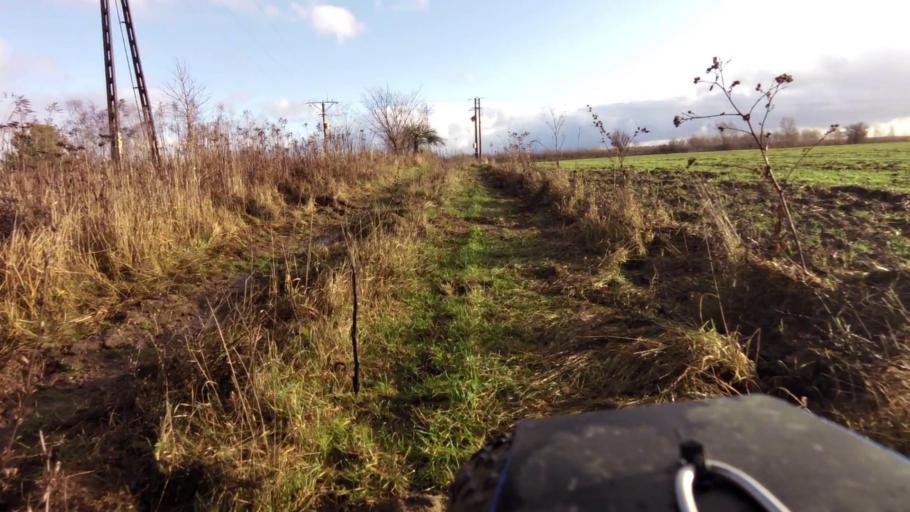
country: PL
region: Lubusz
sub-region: Powiat gorzowski
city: Jenin
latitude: 52.7278
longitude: 15.1427
